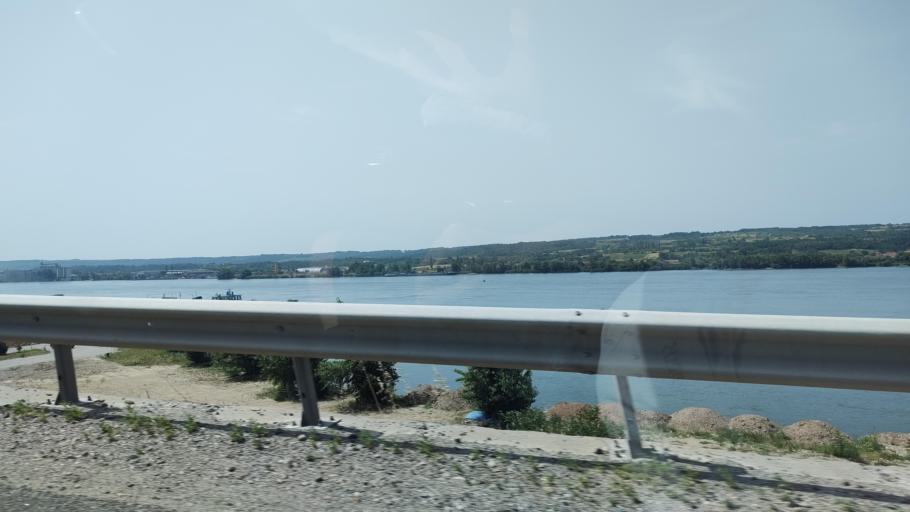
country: RO
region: Mehedinti
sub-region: Municipiul Drobeta-Turnu Severin
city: Gura Vaii
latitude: 44.6367
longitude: 22.5832
